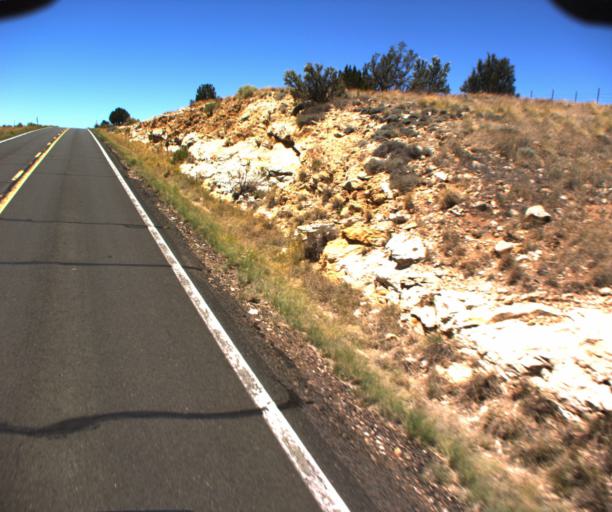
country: US
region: Arizona
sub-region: Coconino County
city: LeChee
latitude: 34.7648
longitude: -111.0149
